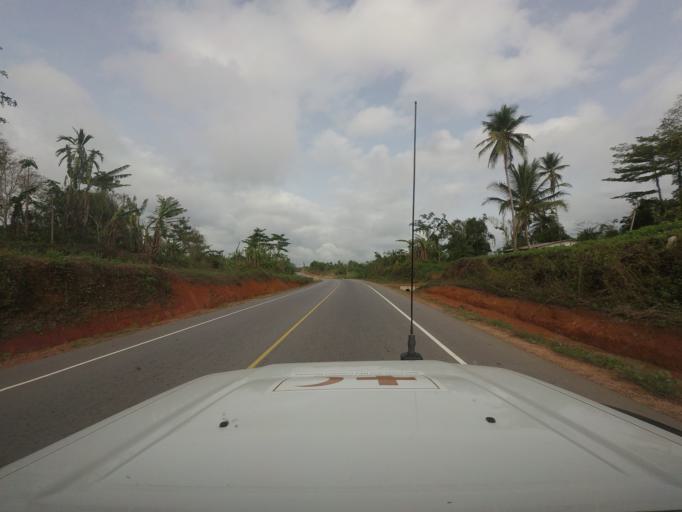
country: LR
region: Bong
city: Gbarnga
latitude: 7.0050
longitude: -9.3033
